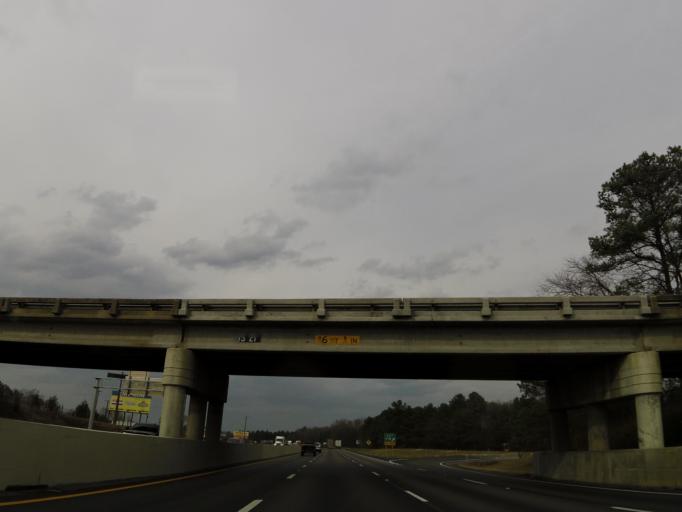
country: US
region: South Carolina
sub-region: Lexington County
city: Pineridge
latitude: 33.8802
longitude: -81.0368
